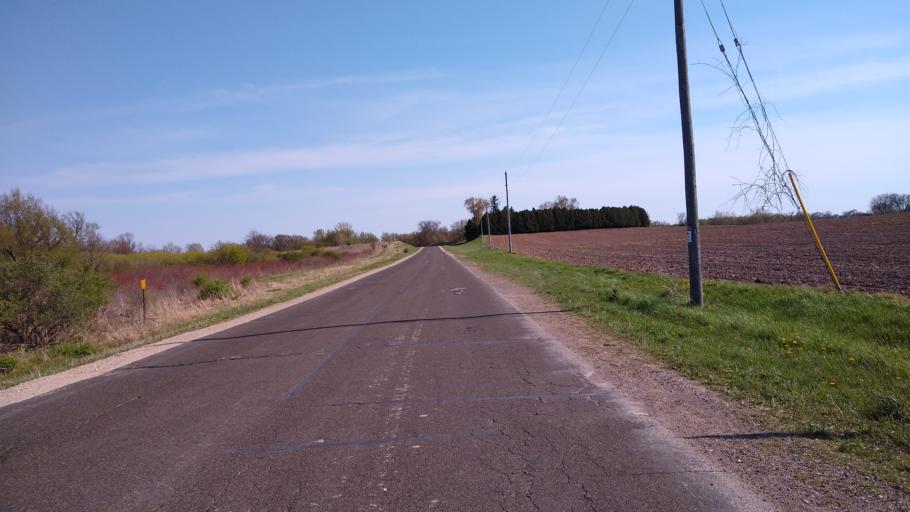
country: US
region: Wisconsin
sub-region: Dane County
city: Waunakee
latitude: 43.1455
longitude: -89.4385
